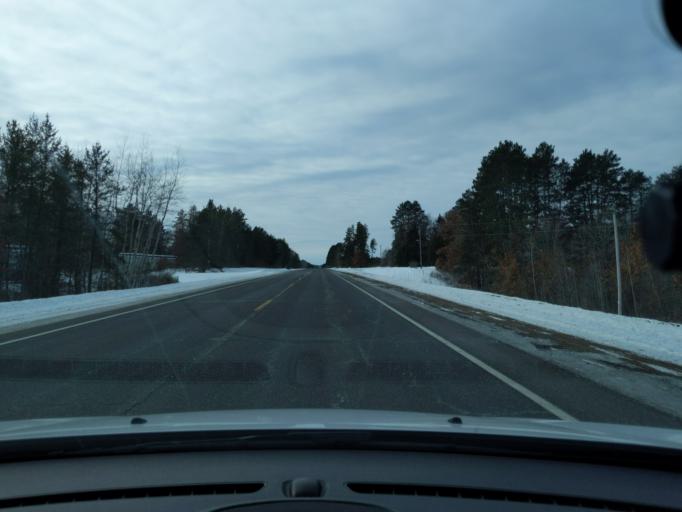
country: US
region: Wisconsin
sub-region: Washburn County
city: Spooner
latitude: 45.9195
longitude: -91.7362
